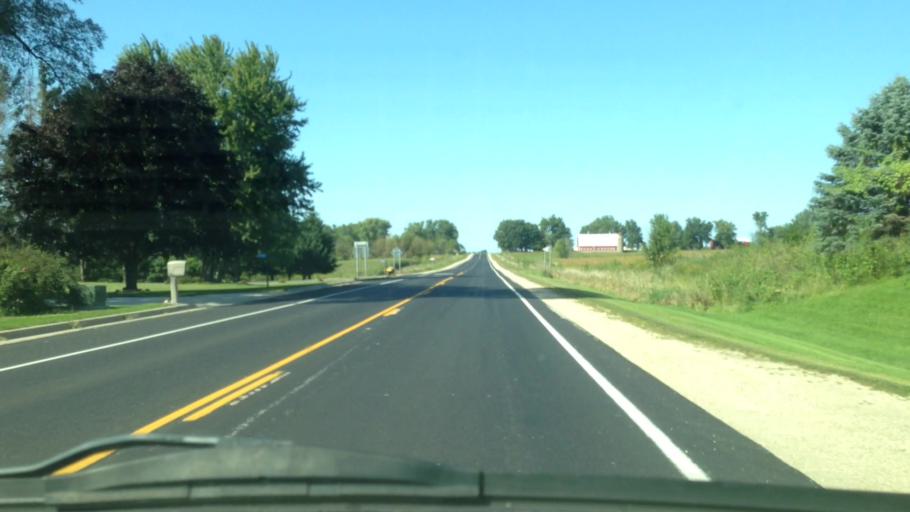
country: US
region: Minnesota
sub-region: Winona County
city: Lewiston
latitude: 43.9410
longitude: -91.7901
